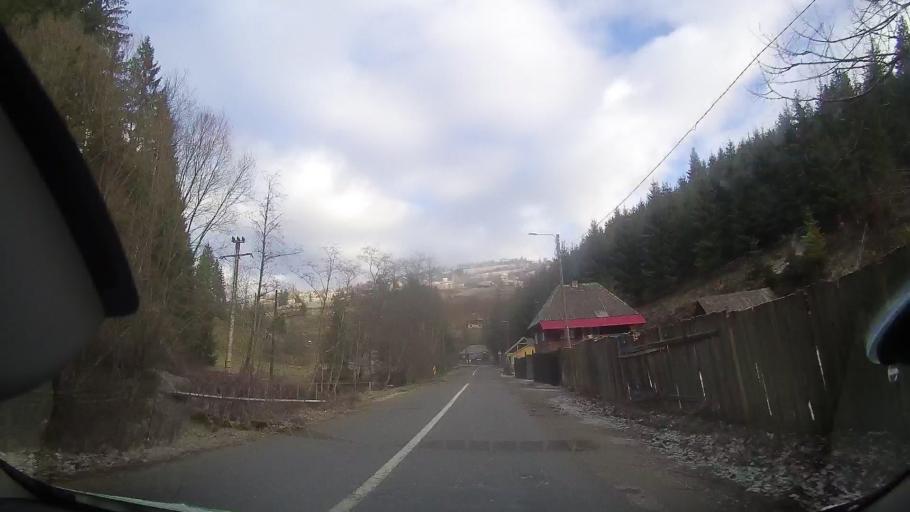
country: RO
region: Alba
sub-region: Comuna Albac
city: Albac
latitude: 46.4677
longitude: 22.9679
